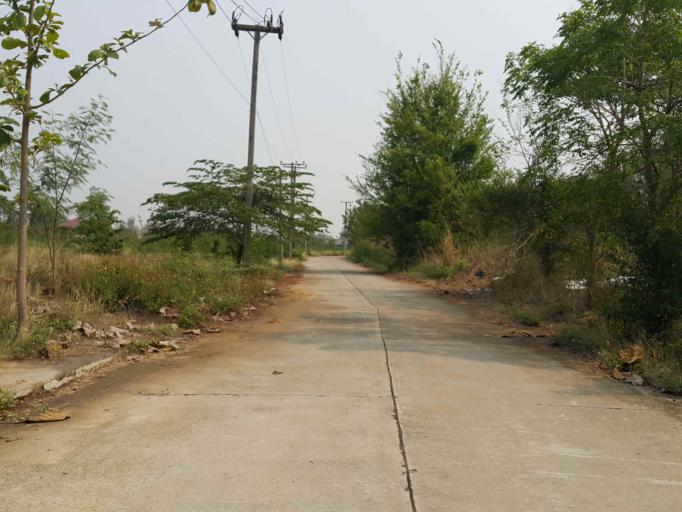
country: TH
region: Chiang Mai
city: Saraphi
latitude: 18.7597
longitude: 99.0597
